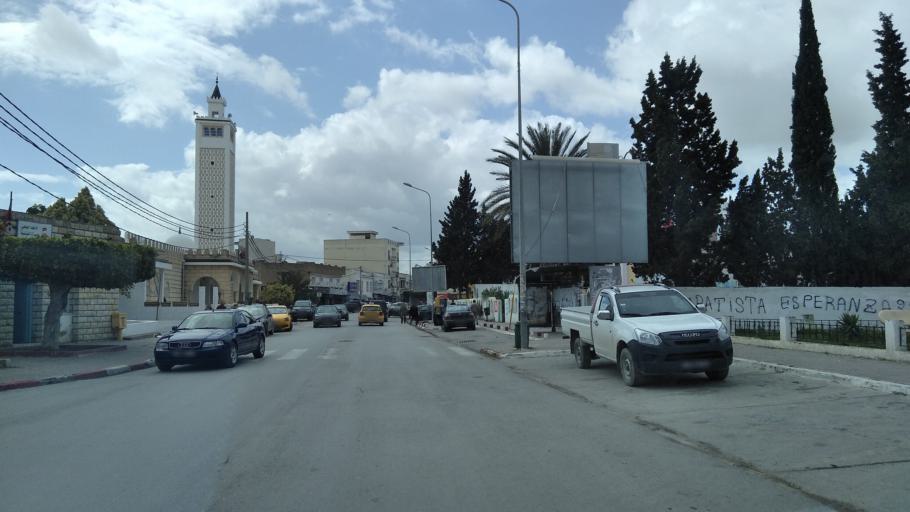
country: TN
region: Bin 'Arus
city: Ben Arous
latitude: 36.7587
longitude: 10.2225
